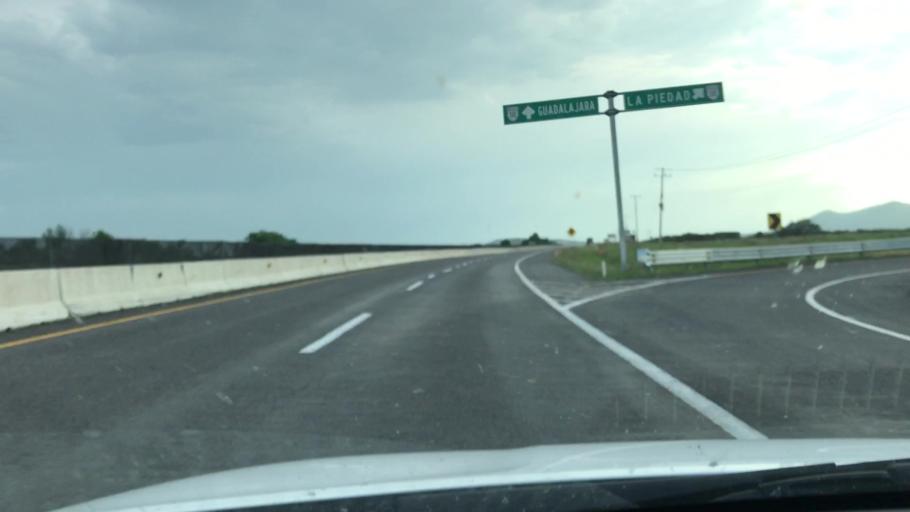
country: MX
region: Jalisco
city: Degollado
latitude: 20.3672
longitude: -102.1301
